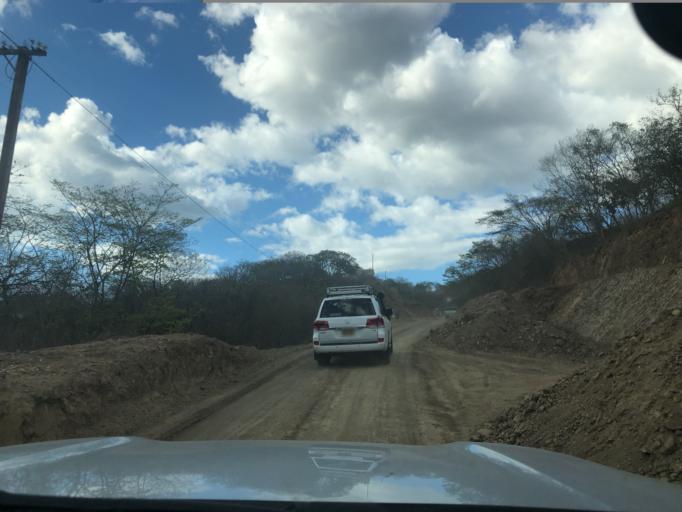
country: NI
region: Nueva Segovia
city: Ocotal
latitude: 13.6549
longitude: -86.6148
